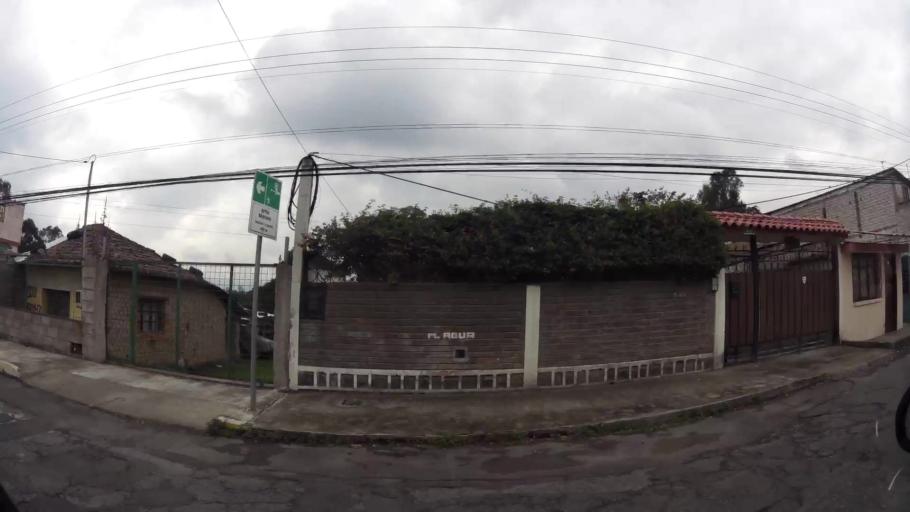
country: EC
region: Pichincha
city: Sangolqui
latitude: -0.3012
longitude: -78.4688
